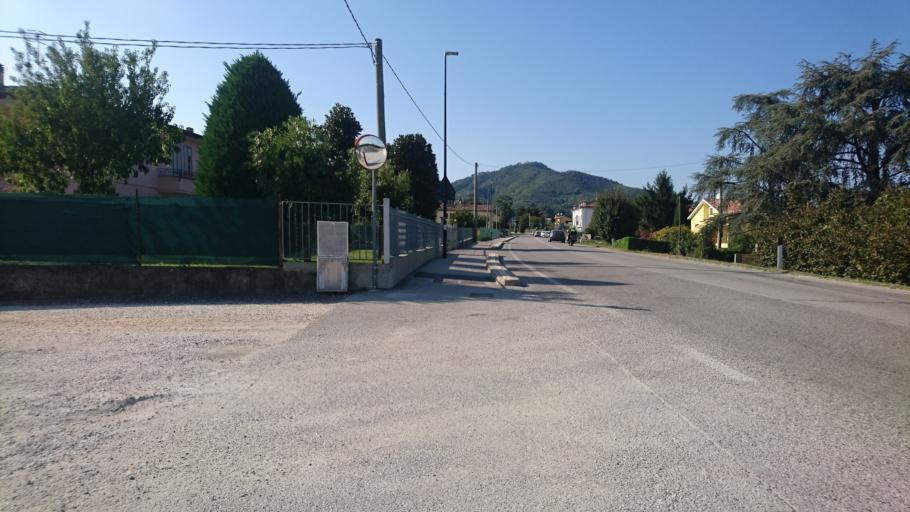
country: IT
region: Veneto
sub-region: Provincia di Padova
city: Galzignano
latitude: 45.3041
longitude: 11.7450
